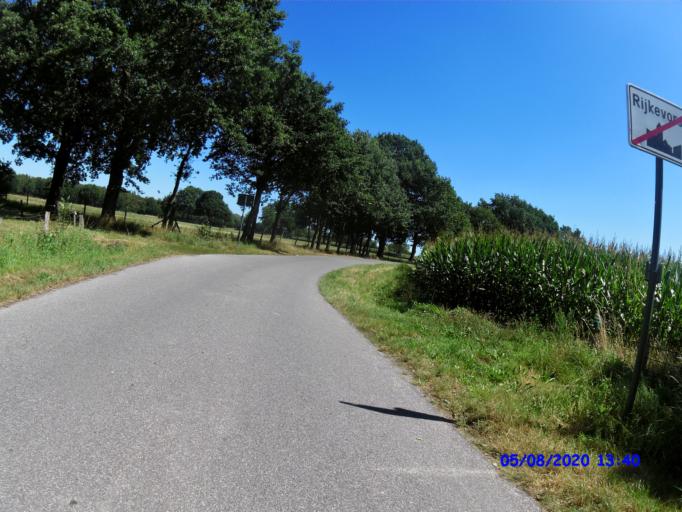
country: BE
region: Flanders
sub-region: Provincie Antwerpen
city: Rijkevorsel
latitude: 51.3598
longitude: 4.7697
